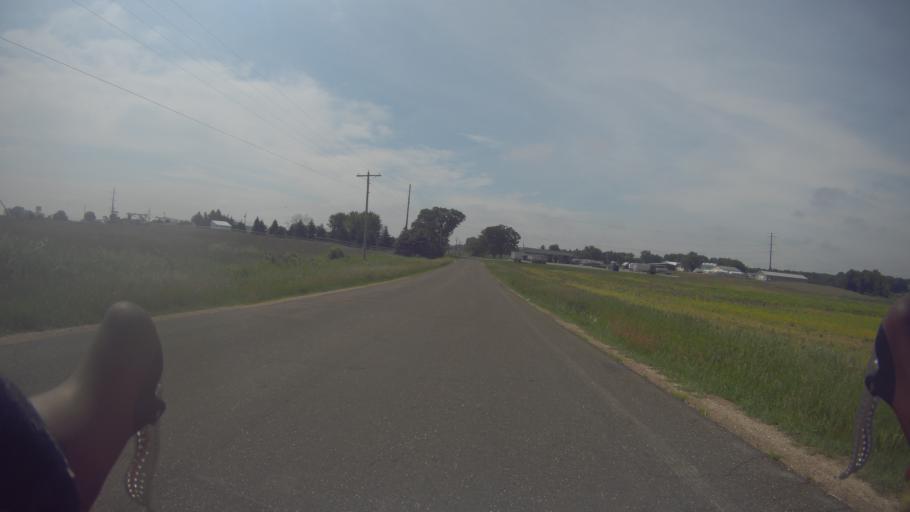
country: US
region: Wisconsin
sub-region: Rock County
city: Edgerton
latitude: 42.8688
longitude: -89.0535
